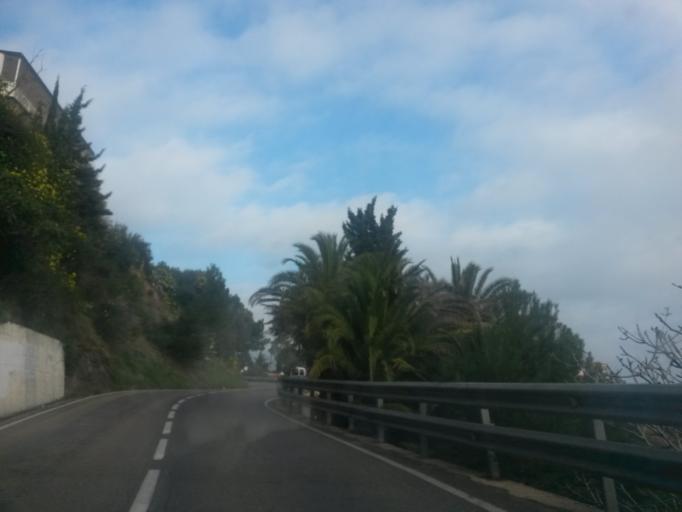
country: ES
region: Catalonia
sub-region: Provincia de Girona
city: Llanca
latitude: 42.3603
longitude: 3.1620
